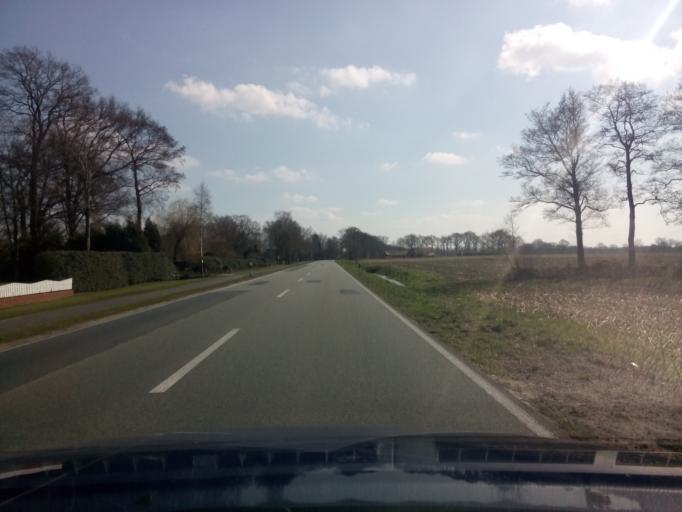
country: DE
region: Lower Saxony
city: Golenkamp
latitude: 52.5352
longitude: 6.9374
